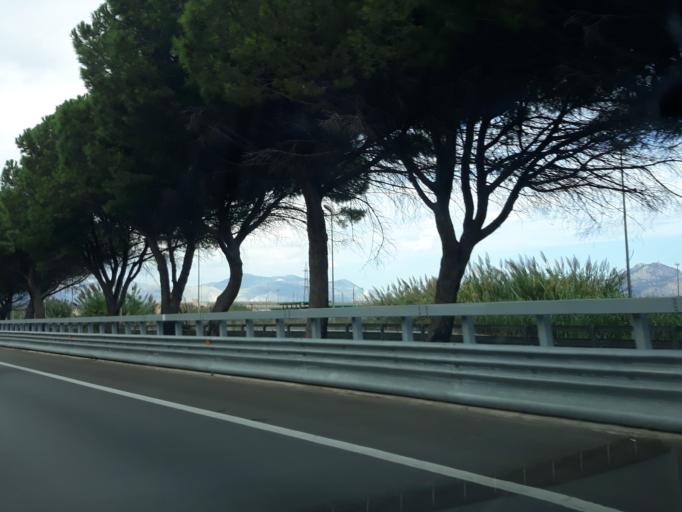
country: IT
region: Sicily
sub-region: Palermo
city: Ciaculli
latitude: 38.0862
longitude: 13.4097
